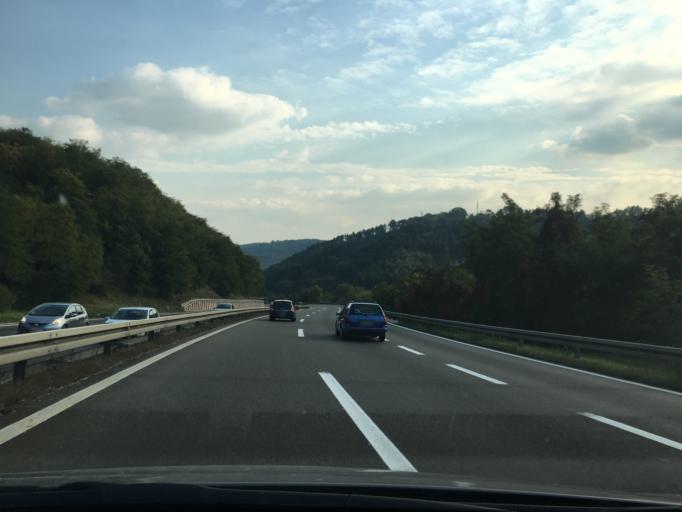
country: RS
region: Central Serbia
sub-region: Belgrade
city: Zvezdara
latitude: 44.7459
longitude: 20.5416
